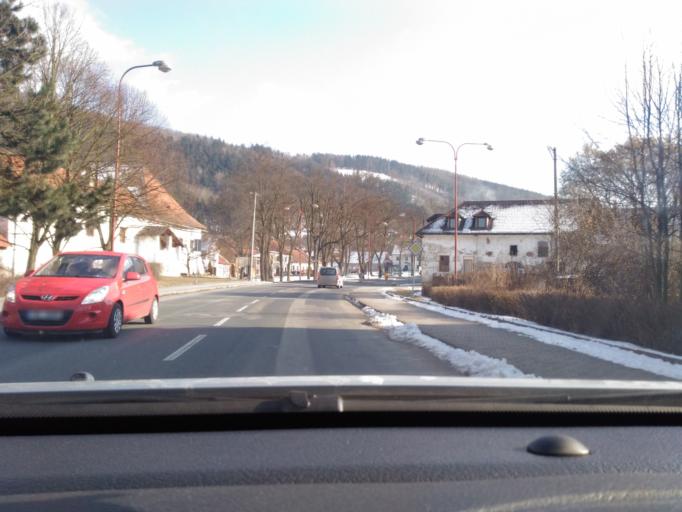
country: CZ
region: South Moravian
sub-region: Okres Brno-Venkov
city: Nedvedice
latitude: 49.4256
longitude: 16.3508
